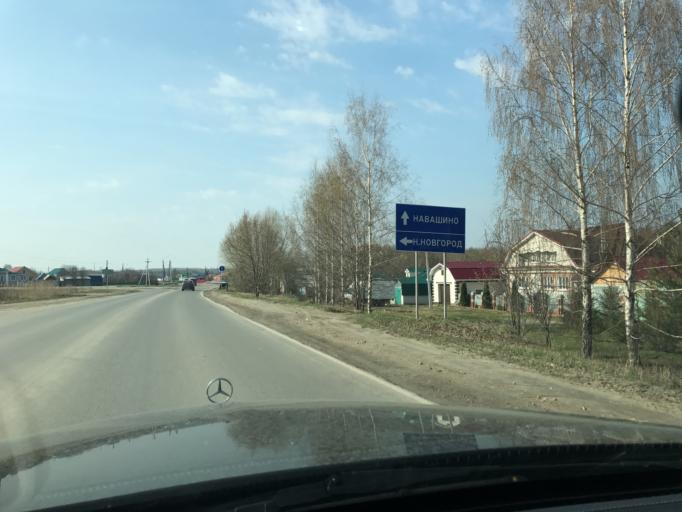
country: RU
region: Nizjnij Novgorod
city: Taremskoye
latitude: 55.9353
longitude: 43.0456
